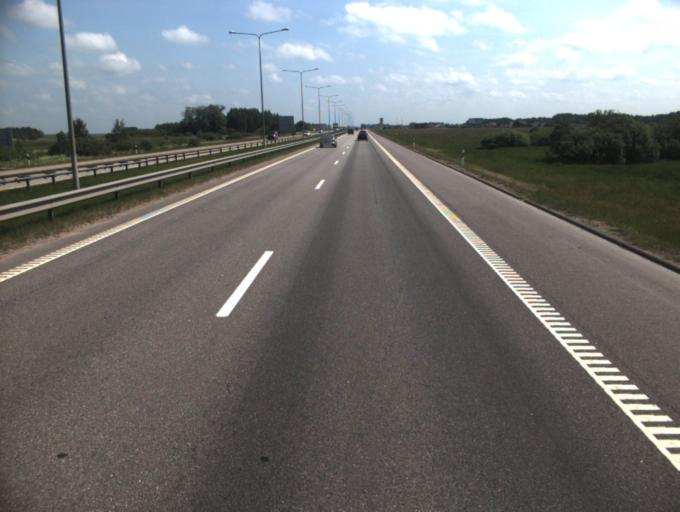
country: LT
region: Klaipedos apskritis
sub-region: Klaipeda
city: Klaipeda
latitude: 55.7100
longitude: 21.2543
